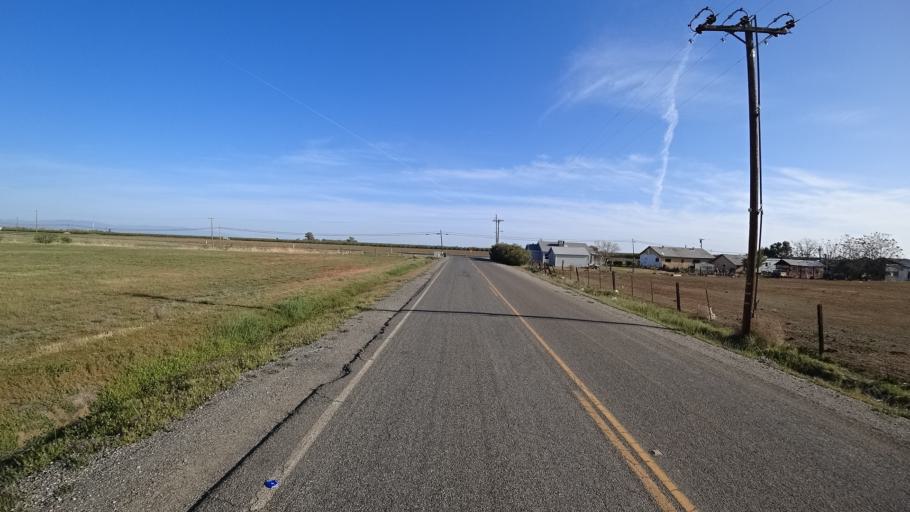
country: US
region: California
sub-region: Glenn County
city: Willows
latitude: 39.5234
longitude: -122.2267
